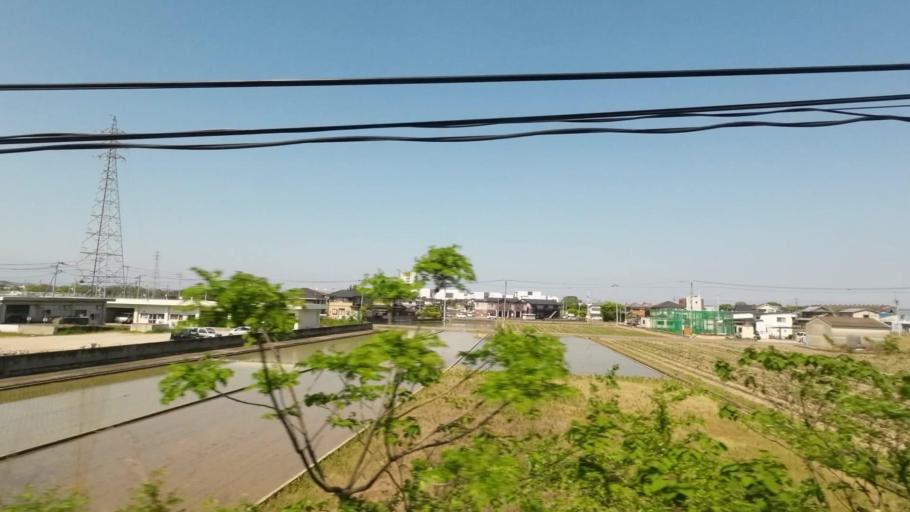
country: JP
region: Kagawa
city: Kan'onjicho
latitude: 34.1178
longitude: 133.6474
